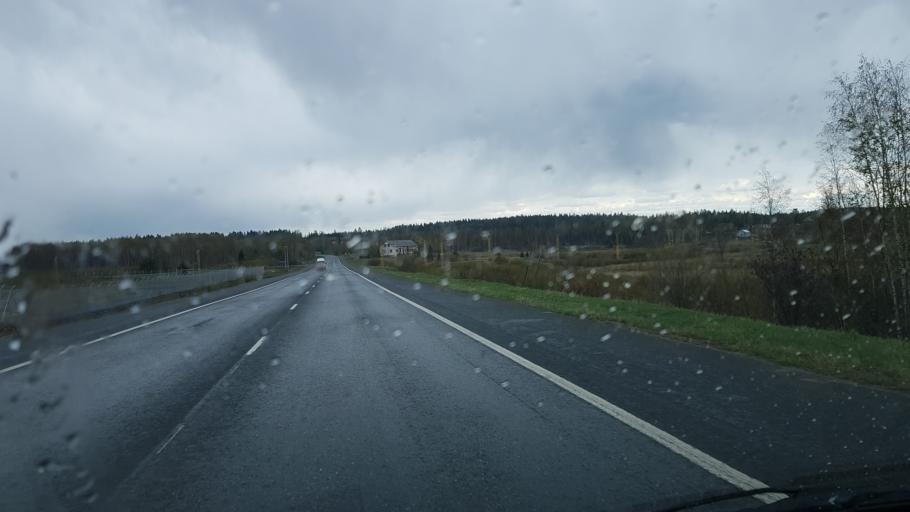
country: FI
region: Pirkanmaa
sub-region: Tampere
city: Pirkkala
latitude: 61.4191
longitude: 23.6344
